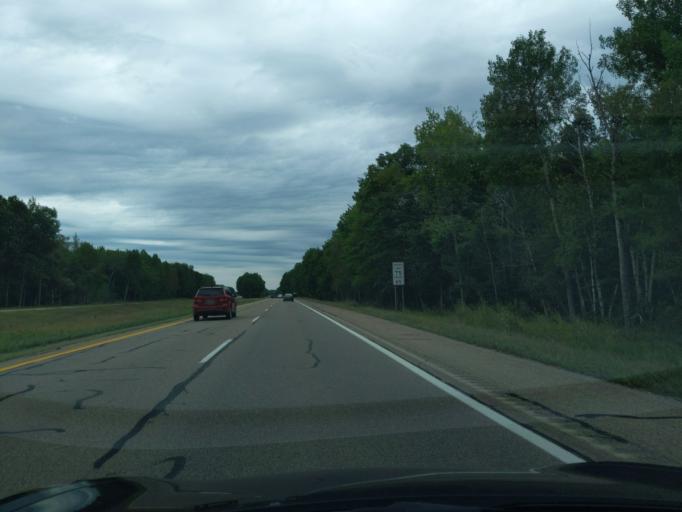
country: US
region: Michigan
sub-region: Roscommon County
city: Houghton Lake
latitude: 44.3264
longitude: -84.8074
